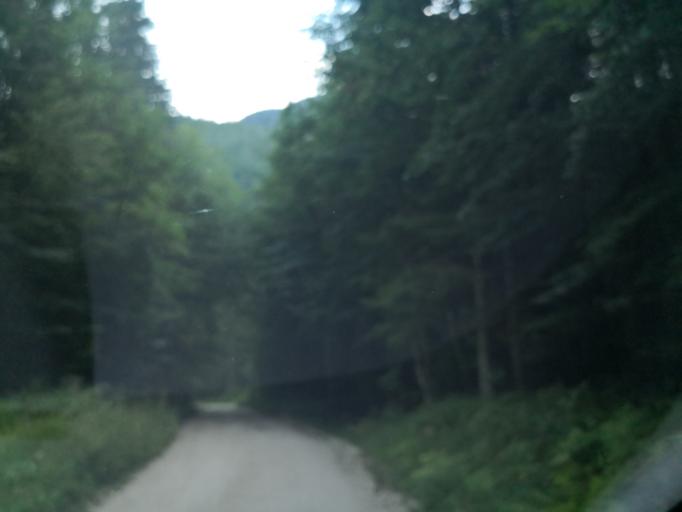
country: SI
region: Jezersko
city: Zgornje Jezersko
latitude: 46.3894
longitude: 14.5329
